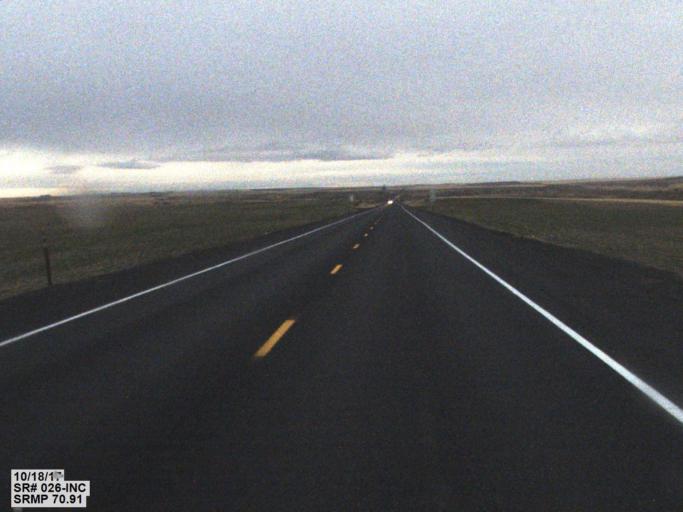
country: US
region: Washington
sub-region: Franklin County
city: Connell
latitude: 46.7949
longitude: -118.5406
